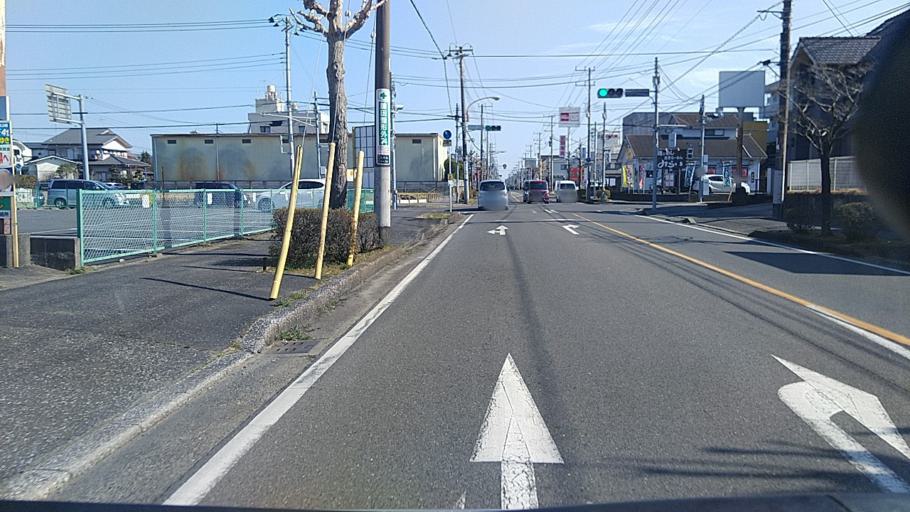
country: JP
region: Chiba
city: Mobara
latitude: 35.4238
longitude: 140.2928
